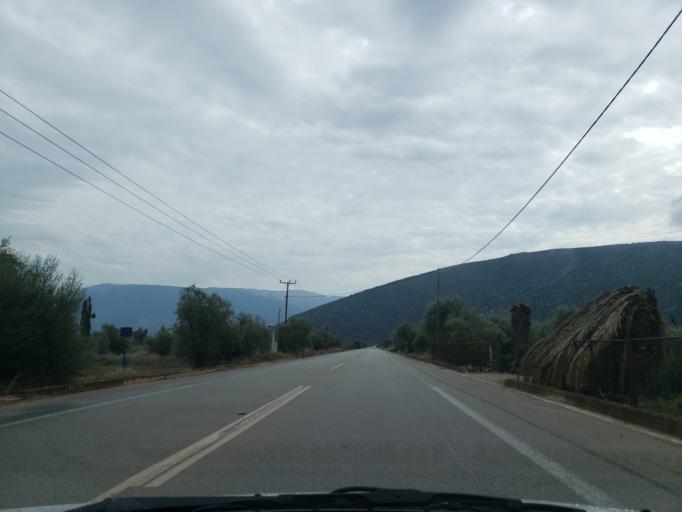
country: GR
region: Central Greece
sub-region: Nomos Fokidos
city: Amfissa
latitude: 38.4901
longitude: 22.4169
